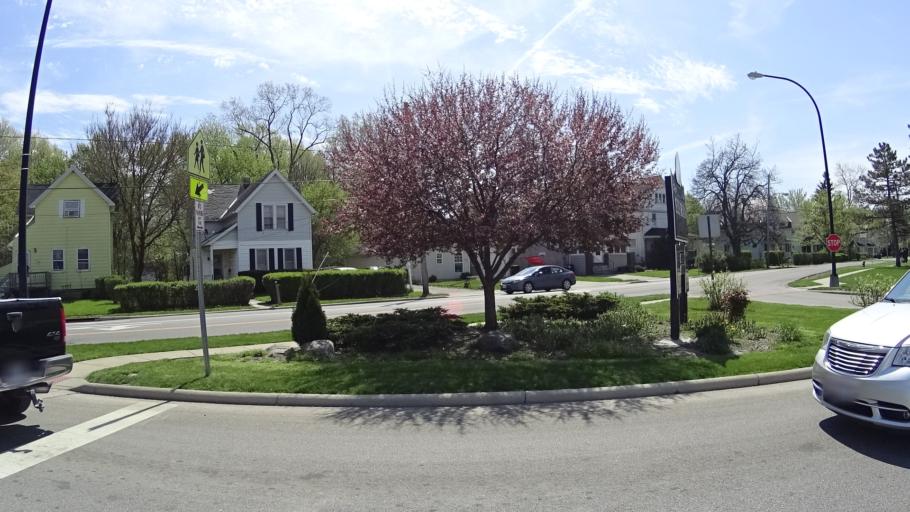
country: US
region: Ohio
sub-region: Lorain County
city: Elyria
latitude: 41.3508
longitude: -82.1077
